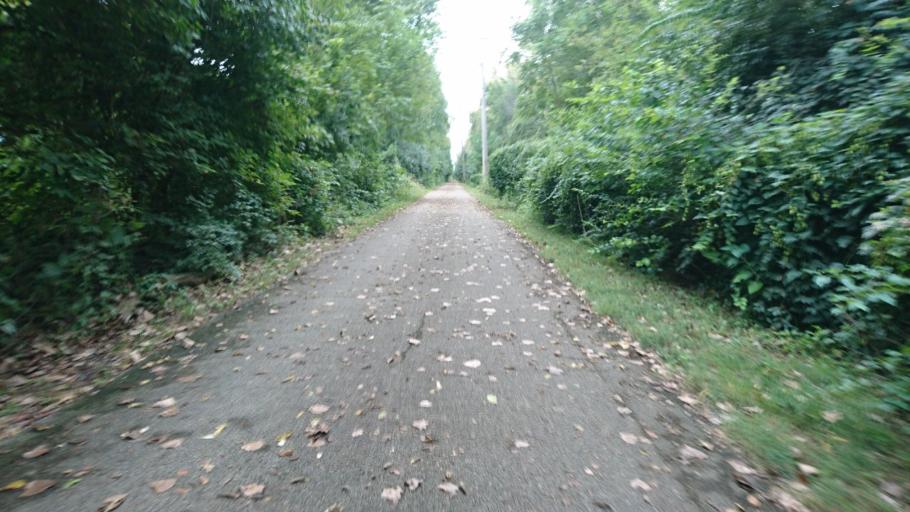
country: US
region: Illinois
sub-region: Sangamon County
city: Southern View
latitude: 39.7341
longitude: -89.6719
